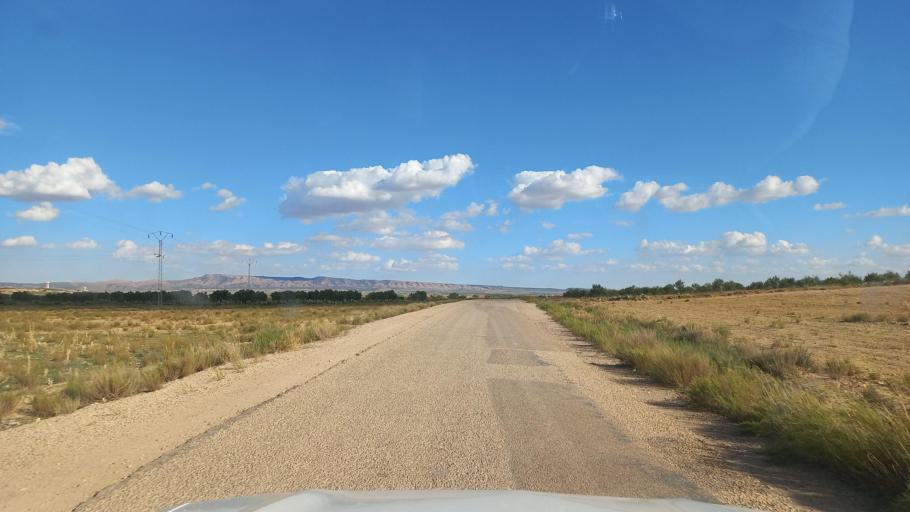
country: TN
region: Al Qasrayn
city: Sbiba
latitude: 35.3920
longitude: 9.0240
